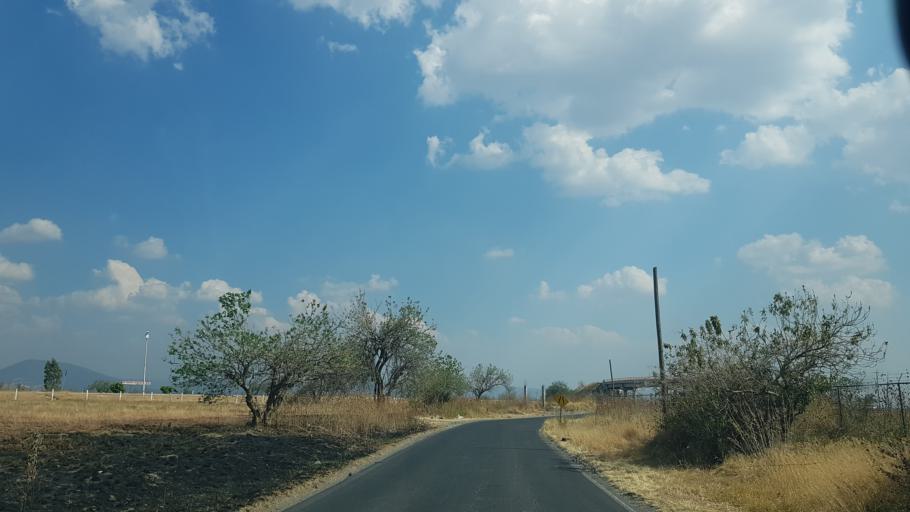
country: MX
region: Puebla
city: Atlixco
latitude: 18.9228
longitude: -98.4832
